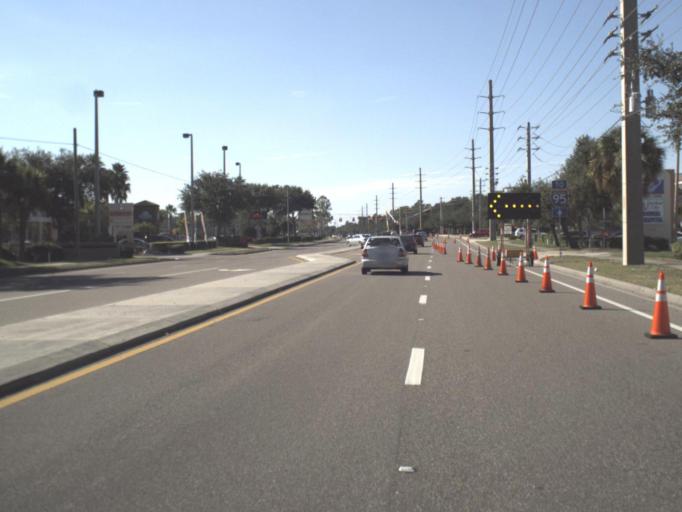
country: US
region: Florida
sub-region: Brevard County
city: South Patrick Shores
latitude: 28.2307
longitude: -80.6954
